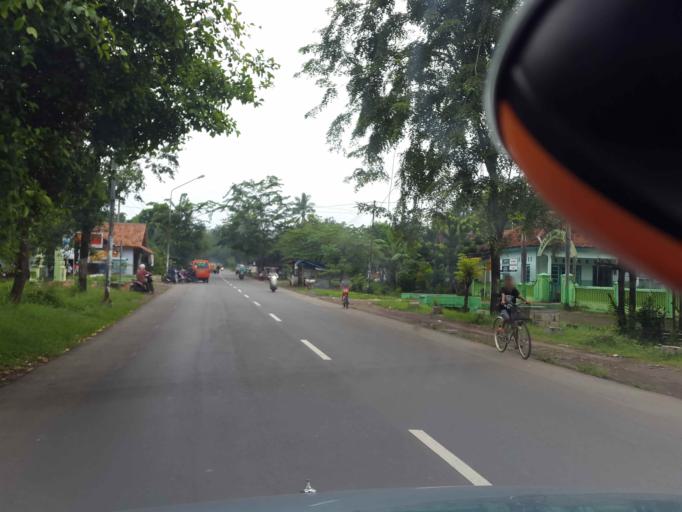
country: ID
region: Central Java
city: Wonopringgo
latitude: -7.0047
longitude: 109.6345
